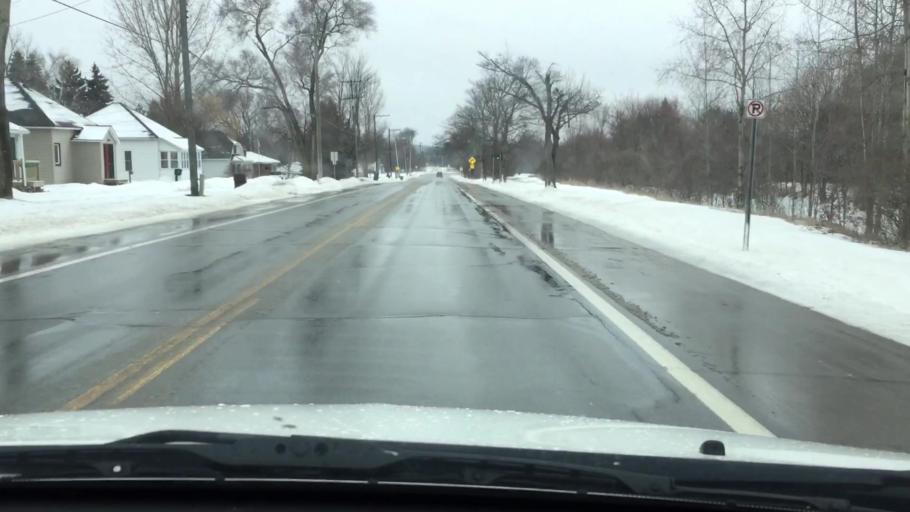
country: US
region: Michigan
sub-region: Wexford County
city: Cadillac
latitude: 44.2367
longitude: -85.4114
